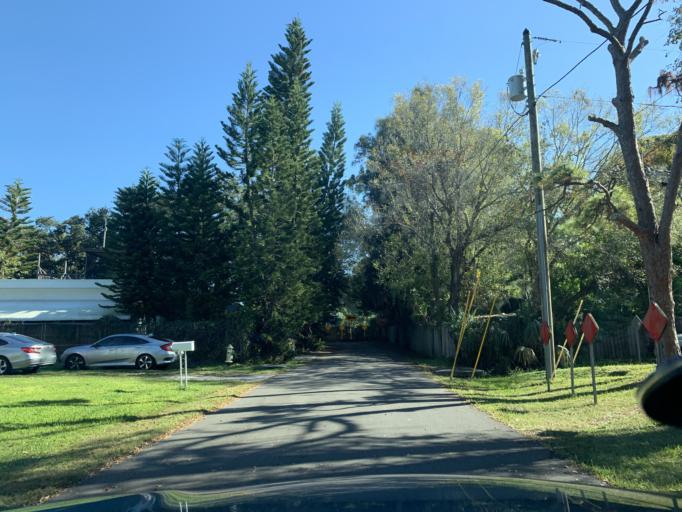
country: US
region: Florida
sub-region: Pinellas County
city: Kenneth City
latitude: 27.8156
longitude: -82.7484
